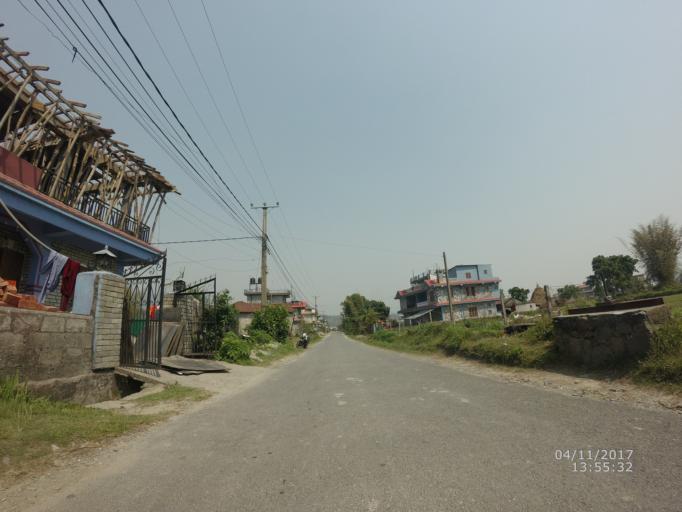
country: NP
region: Western Region
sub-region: Gandaki Zone
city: Pokhara
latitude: 28.1849
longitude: 84.0406
